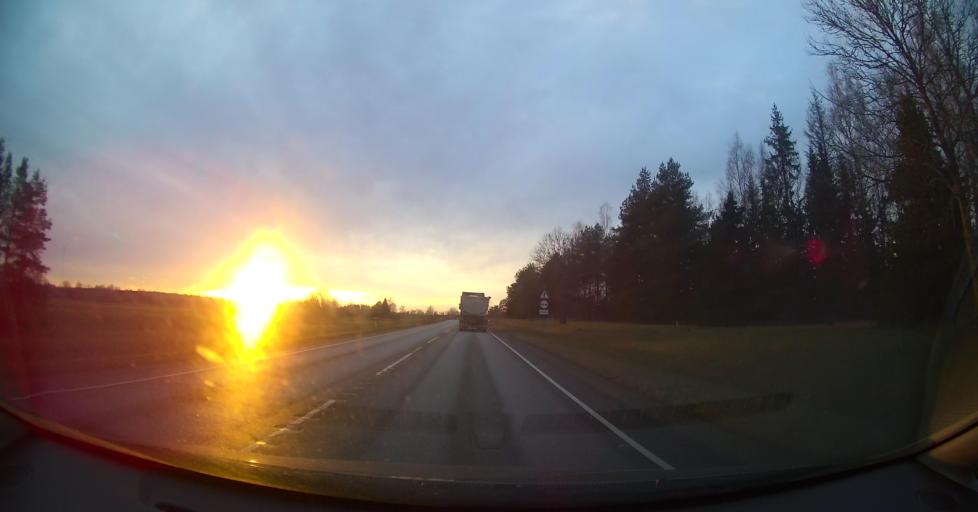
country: EE
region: Ida-Virumaa
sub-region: Aseri vald
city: Aseri
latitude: 59.4351
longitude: 26.7192
